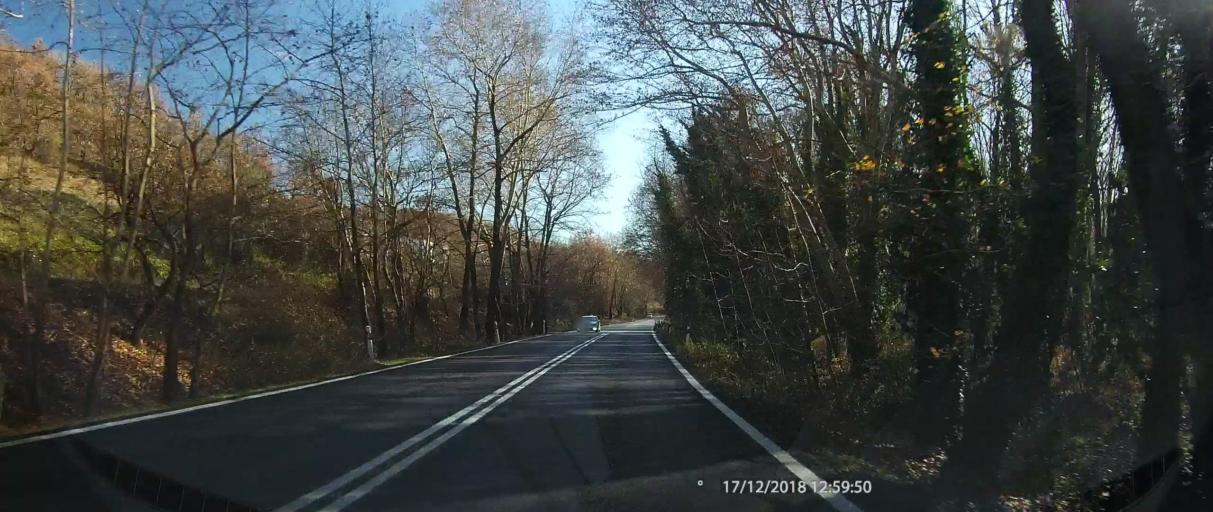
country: GR
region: Thessaly
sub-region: Trikala
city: Kastraki
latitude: 39.7338
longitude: 21.5612
